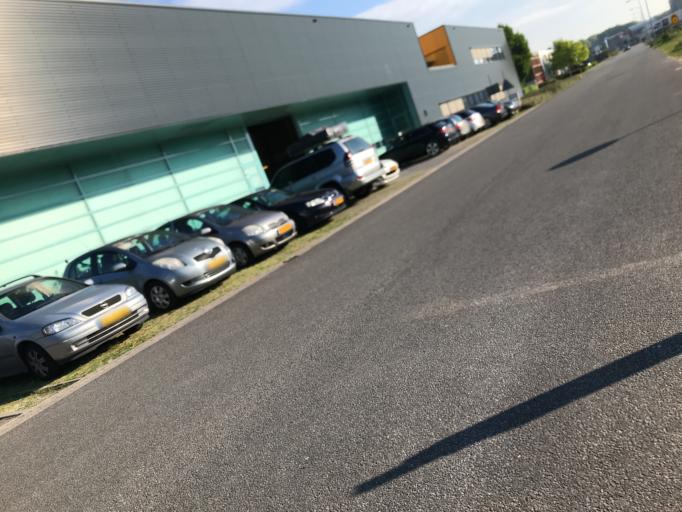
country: NL
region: North Brabant
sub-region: Gemeente Eindhoven
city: Meerhoven
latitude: 51.4506
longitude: 5.3944
